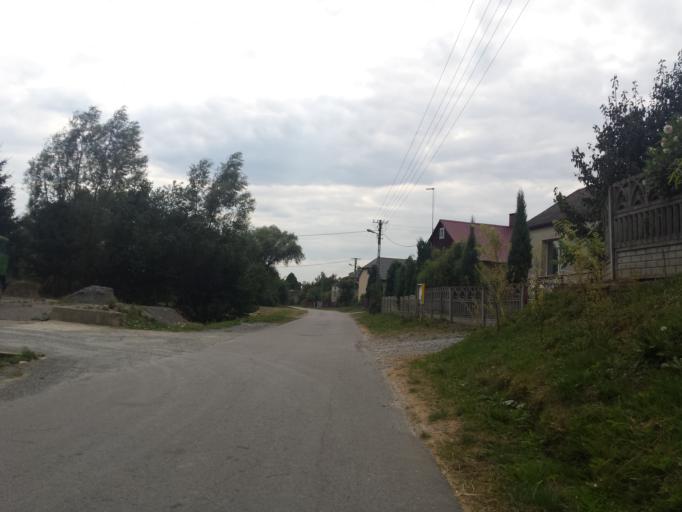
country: PL
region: Swietokrzyskie
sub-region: Powiat staszowski
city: Bogoria
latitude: 50.6646
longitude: 21.2363
